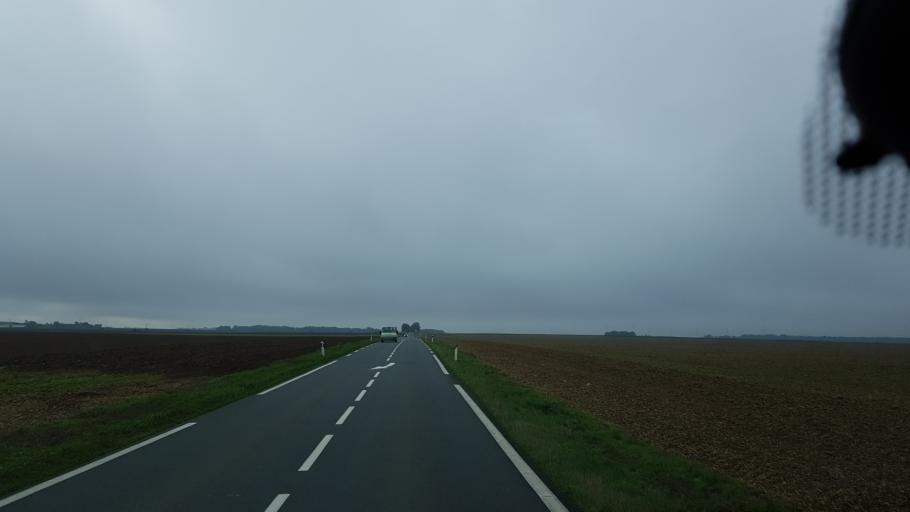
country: FR
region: Ile-de-France
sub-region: Departement de l'Essonne
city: Pussay
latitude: 48.4211
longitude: 1.9643
